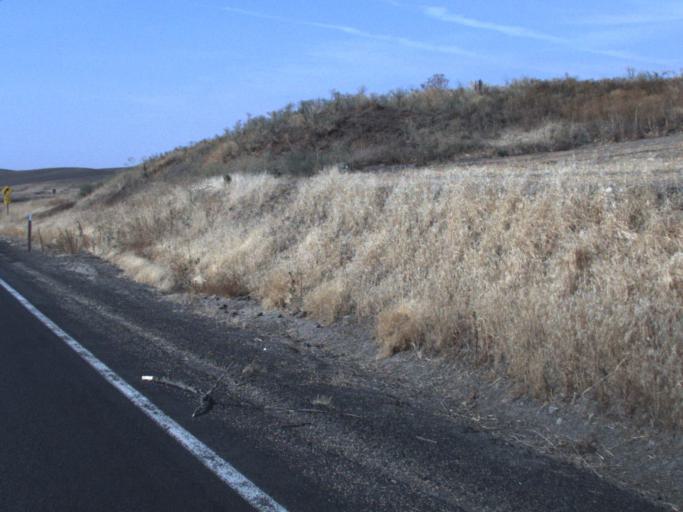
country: US
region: Idaho
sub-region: Benewah County
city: Plummer
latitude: 47.1779
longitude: -117.1839
